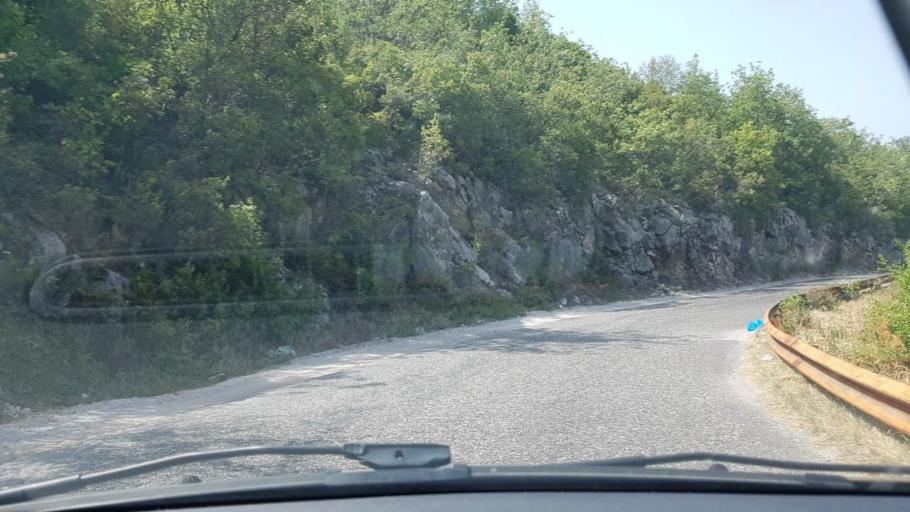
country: BA
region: Federation of Bosnia and Herzegovina
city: Tasovcici
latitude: 43.0136
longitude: 17.7860
